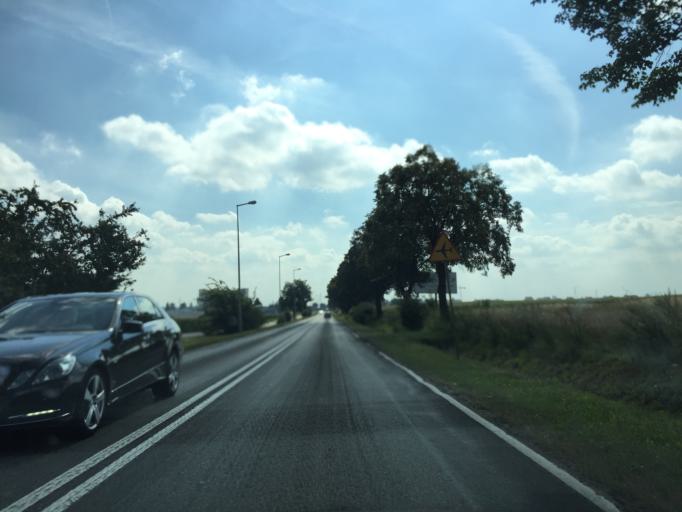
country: PL
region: Greater Poland Voivodeship
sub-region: Kalisz
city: Kalisz
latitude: 51.7675
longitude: 18.0515
